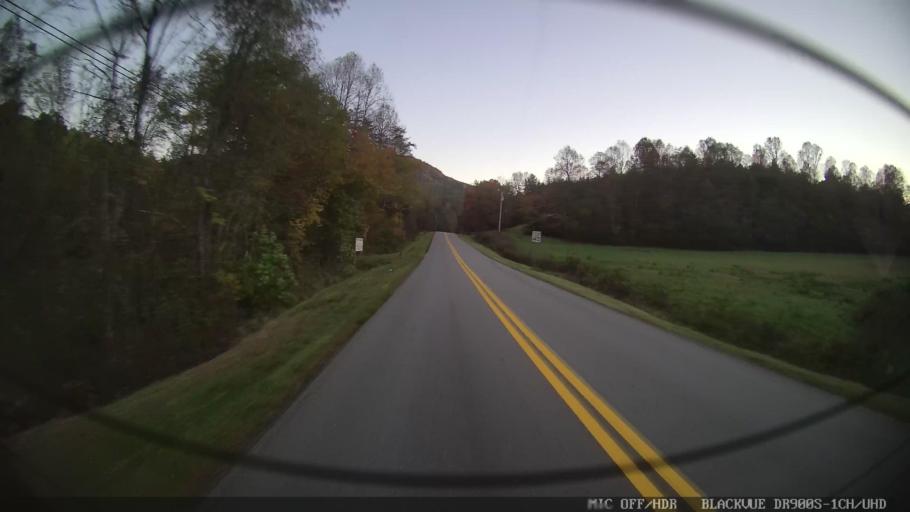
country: US
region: Georgia
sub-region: Union County
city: Blairsville
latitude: 34.9037
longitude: -83.8657
